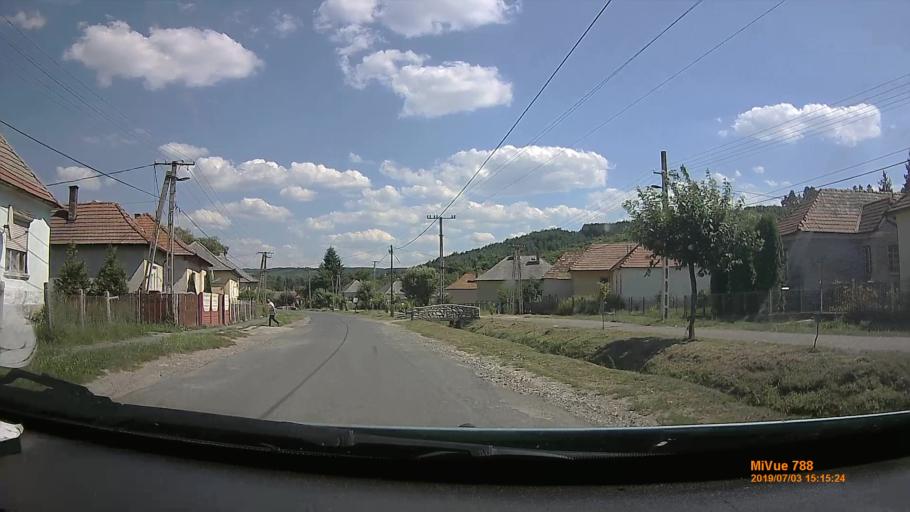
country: HU
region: Borsod-Abauj-Zemplen
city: Farkaslyuk
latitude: 48.2145
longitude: 20.3922
